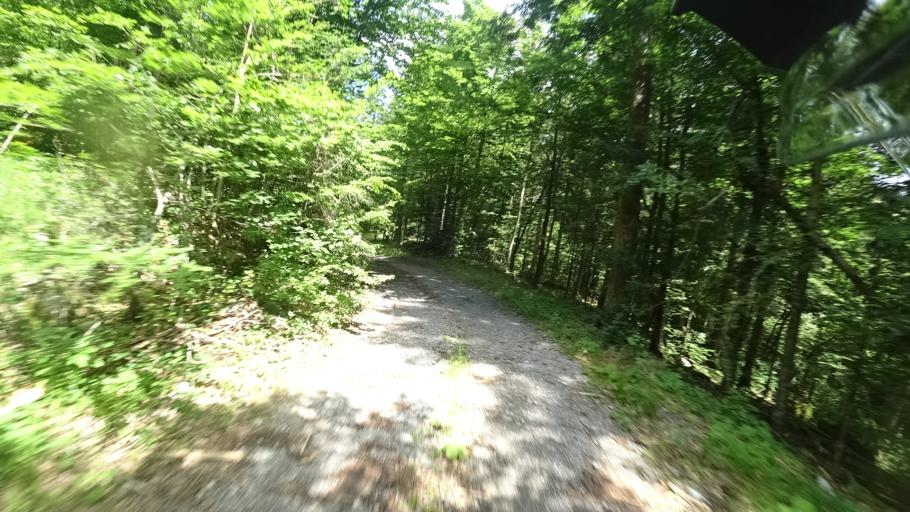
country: SI
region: Osilnica
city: Osilnica
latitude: 45.5395
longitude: 14.5879
